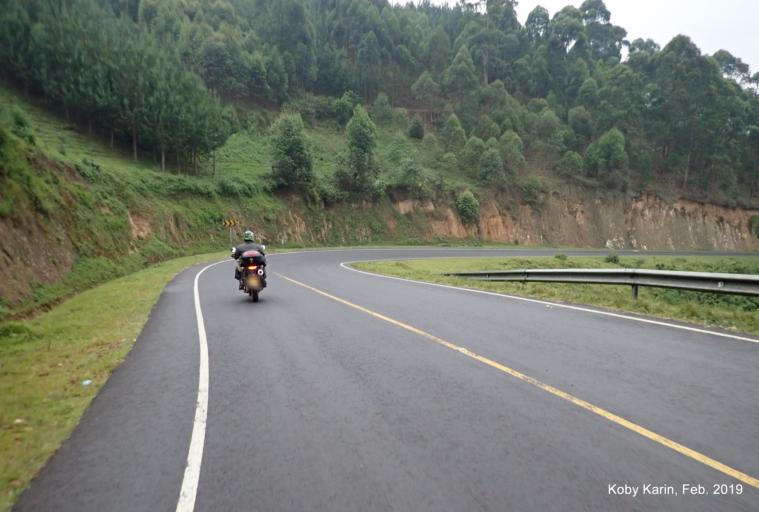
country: UG
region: Western Region
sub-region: Kabale District
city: Kabale
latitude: -1.1954
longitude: 29.8356
